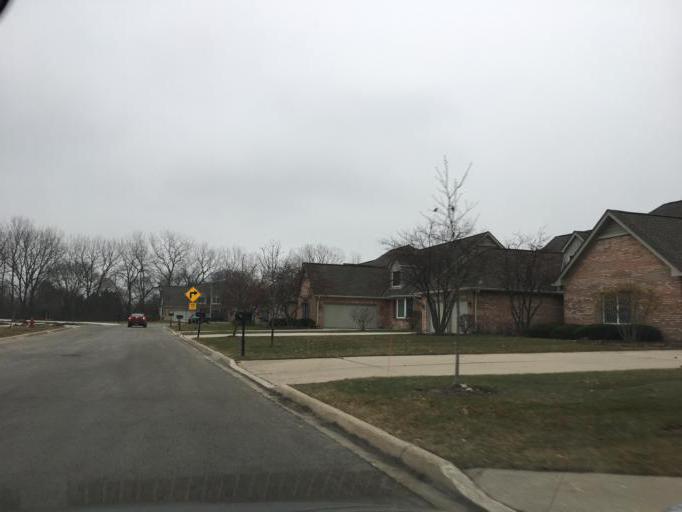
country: US
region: Illinois
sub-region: McHenry County
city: Lakewood
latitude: 42.2254
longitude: -88.3570
